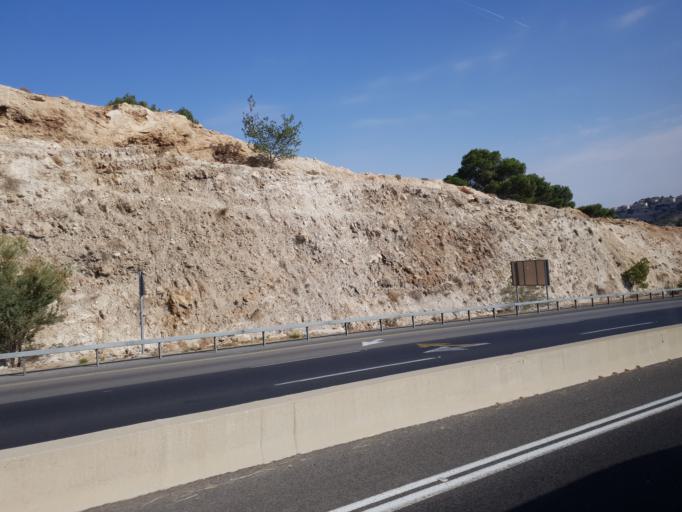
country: PS
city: Az Za`ayyim
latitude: 31.7839
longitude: 35.2854
